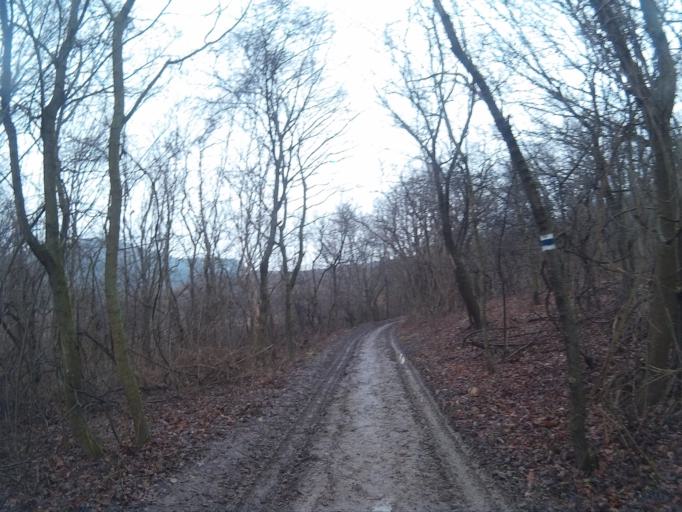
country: HU
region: Komarom-Esztergom
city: Nyergesujfalu
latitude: 47.7215
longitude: 18.5923
